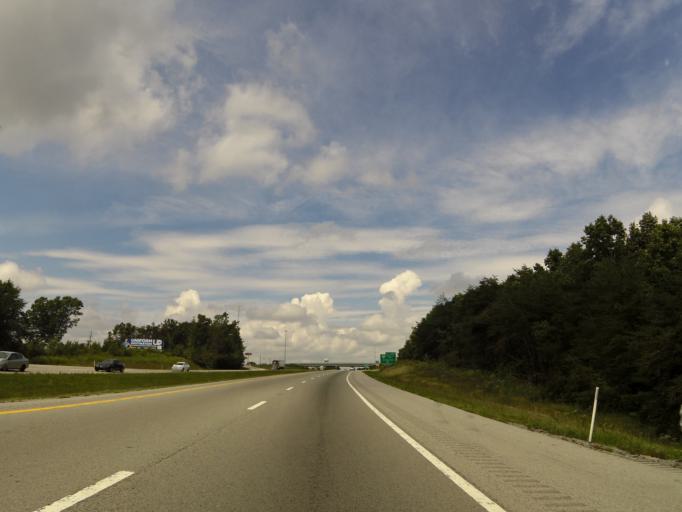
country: US
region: Tennessee
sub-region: Cumberland County
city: Crossville
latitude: 35.9595
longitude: -84.9782
